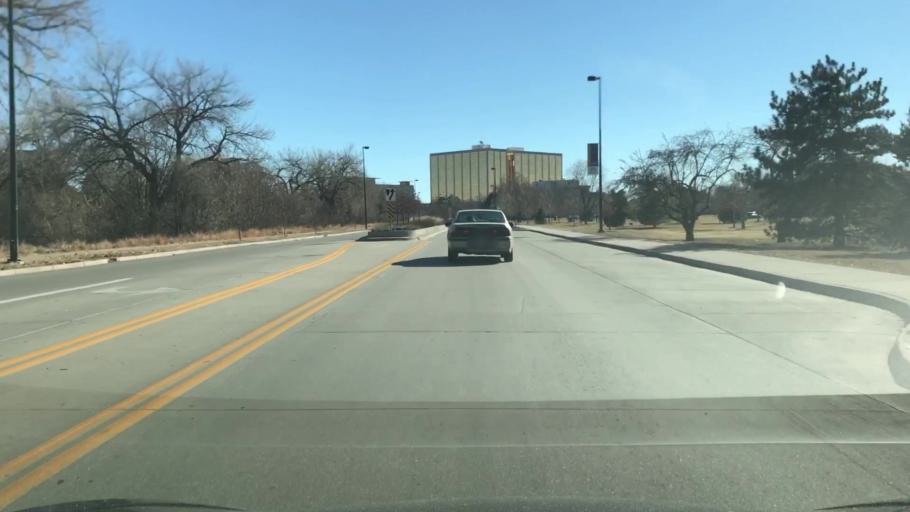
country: US
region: Colorado
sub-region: Arapahoe County
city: Glendale
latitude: 39.7091
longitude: -104.9458
